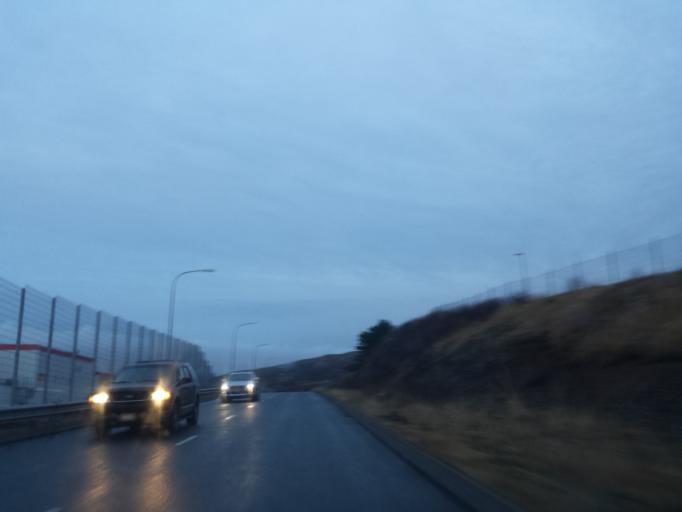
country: IS
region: Capital Region
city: Mosfellsbaer
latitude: 64.1392
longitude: -21.7530
